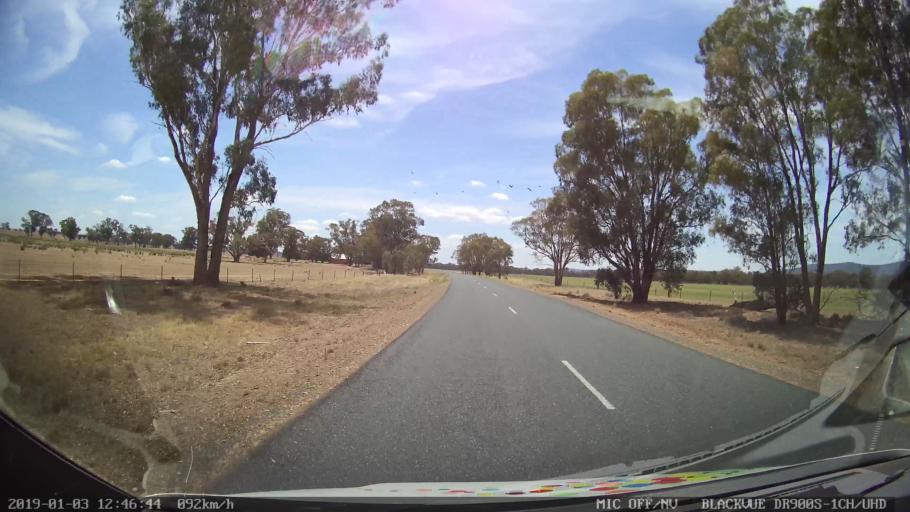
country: AU
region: New South Wales
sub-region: Weddin
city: Grenfell
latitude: -33.7358
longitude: 148.2372
